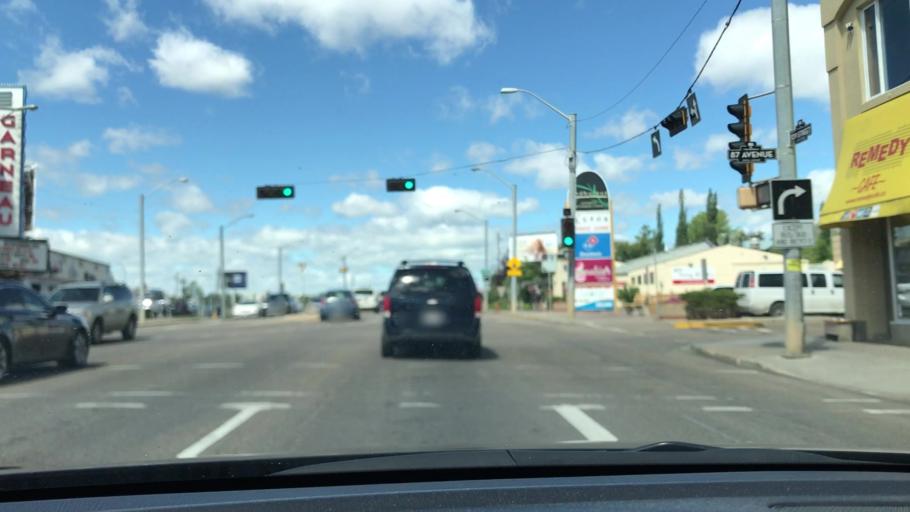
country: CA
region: Alberta
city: Edmonton
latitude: 53.5227
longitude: -113.5120
